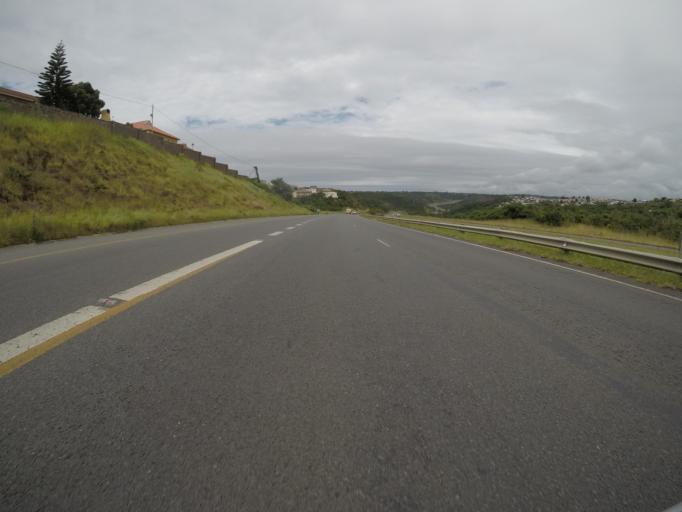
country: ZA
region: Eastern Cape
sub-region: Buffalo City Metropolitan Municipality
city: East London
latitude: -32.9568
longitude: 27.9291
